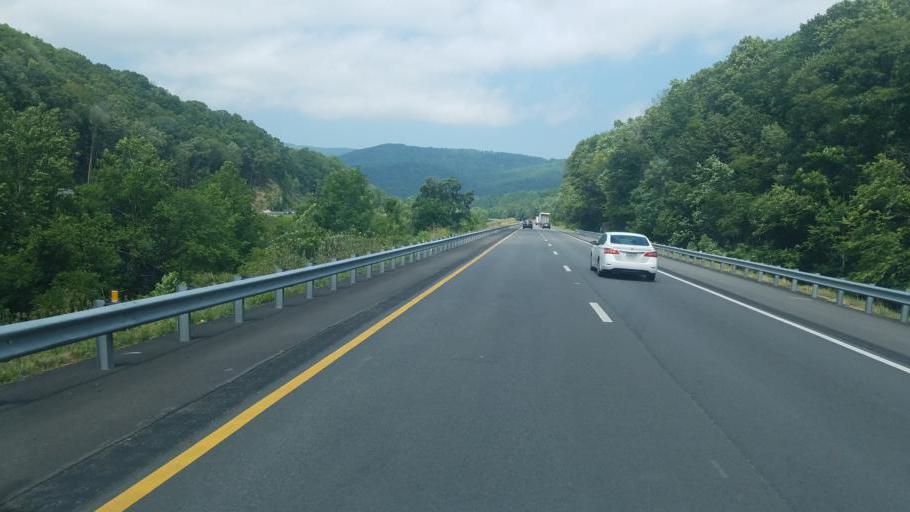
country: US
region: Virginia
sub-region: Bland County
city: Bland
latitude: 37.2278
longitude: -81.0943
